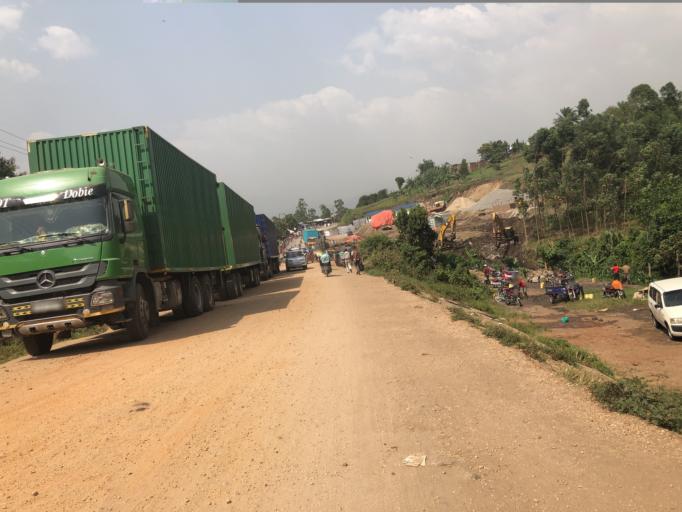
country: UG
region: Western Region
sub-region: Kasese District
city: Kilembe
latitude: 0.0403
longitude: 29.7198
